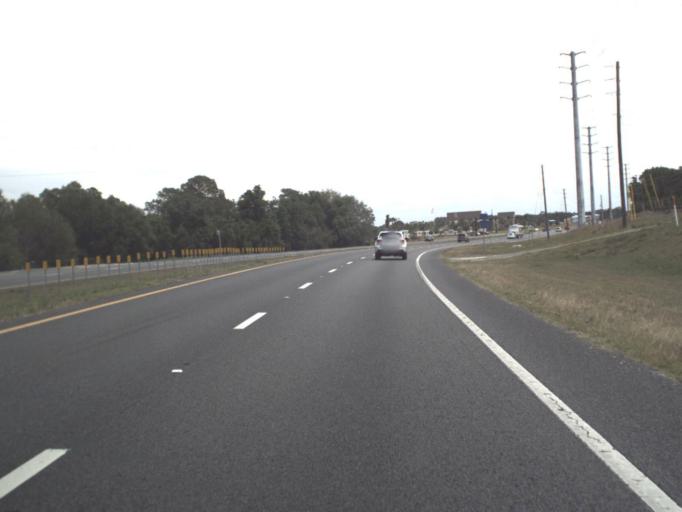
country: US
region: Florida
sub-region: Sumter County
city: Wildwood
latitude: 28.8242
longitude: -81.9785
